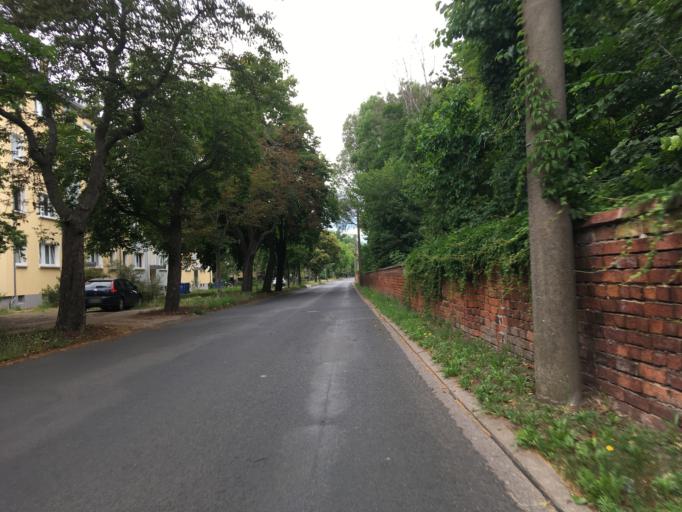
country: DE
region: Saxony-Anhalt
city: Quellendorf
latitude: 51.8077
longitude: 12.1494
